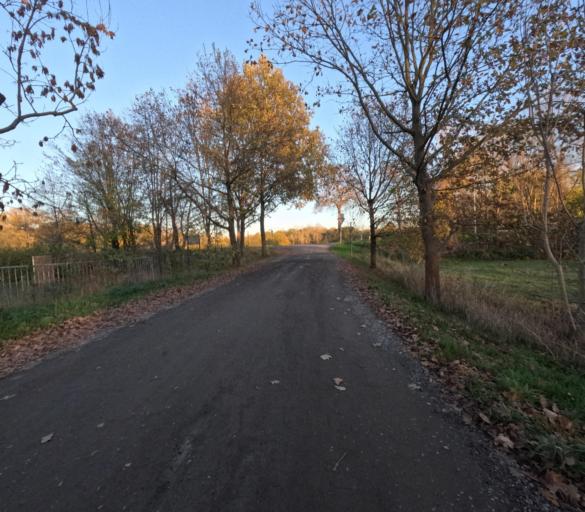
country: DE
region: Saxony
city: Schkeuditz
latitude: 51.3857
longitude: 12.2234
